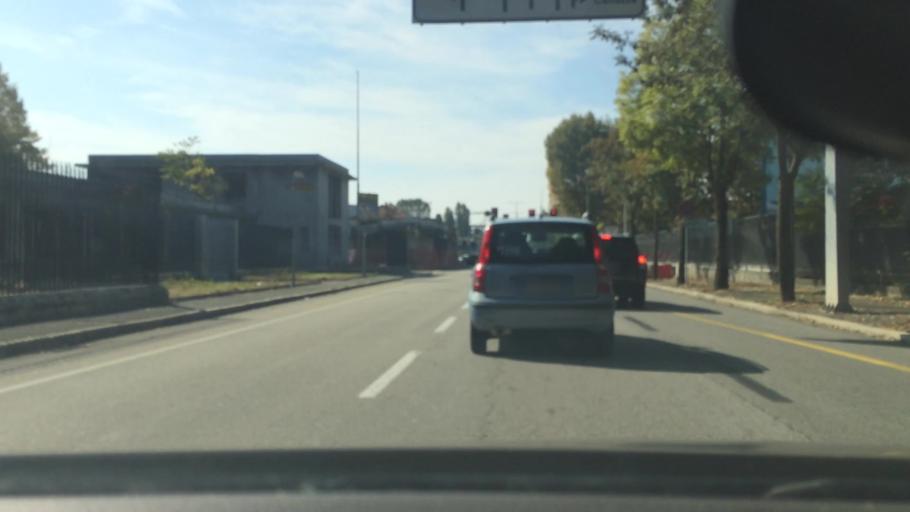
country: IT
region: Lombardy
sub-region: Citta metropolitana di Milano
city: Cerro Maggiore
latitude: 45.6003
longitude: 8.9414
